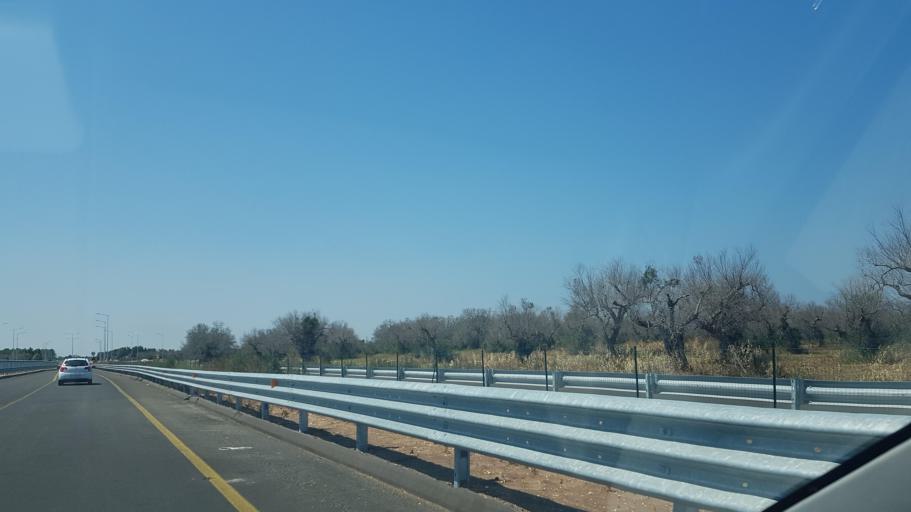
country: IT
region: Apulia
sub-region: Provincia di Lecce
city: Struda
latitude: 40.3234
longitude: 18.2624
